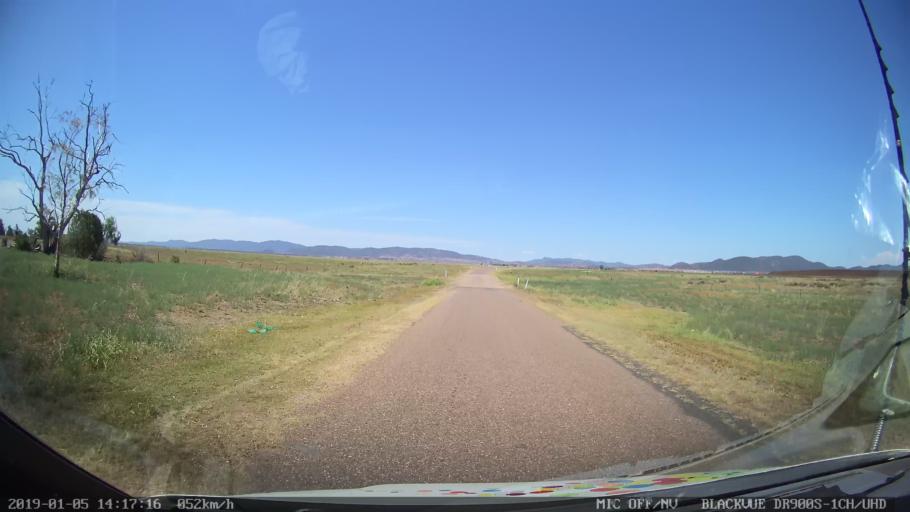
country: AU
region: New South Wales
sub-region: Liverpool Plains
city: Quirindi
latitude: -31.2550
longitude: 150.4759
